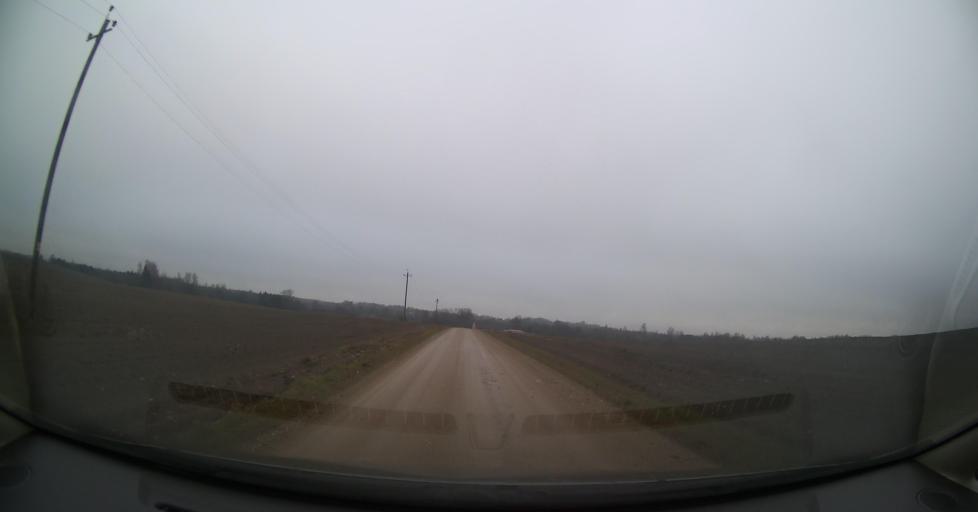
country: EE
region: Tartu
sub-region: Tartu linn
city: Tartu
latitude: 58.3888
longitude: 26.9987
